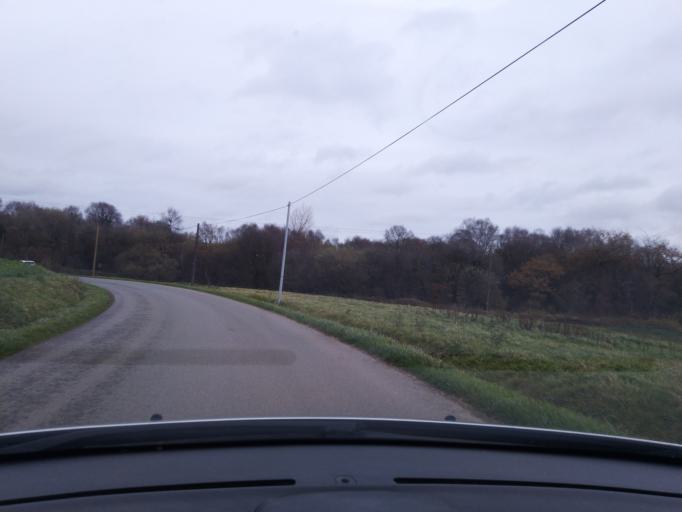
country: FR
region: Brittany
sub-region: Departement du Finistere
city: Guerlesquin
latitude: 48.5535
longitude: -3.5507
